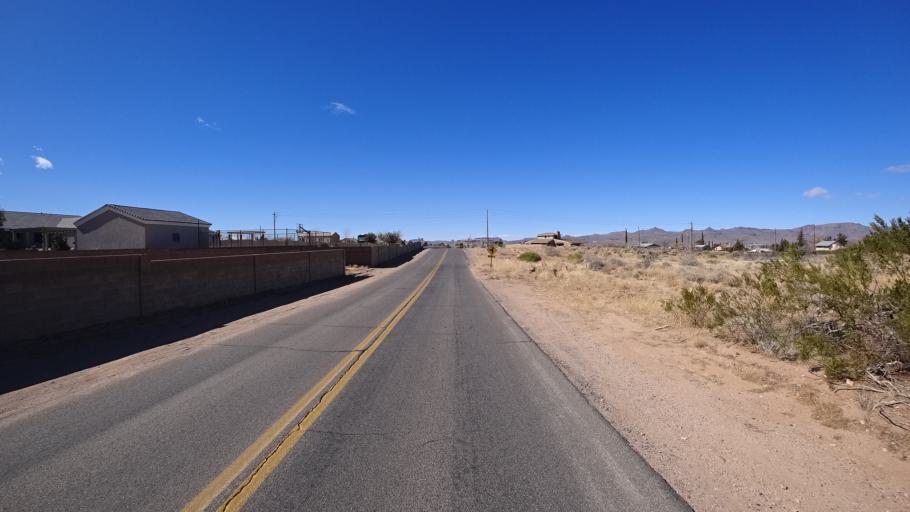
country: US
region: Arizona
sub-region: Mohave County
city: Kingman
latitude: 35.1958
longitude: -114.0014
